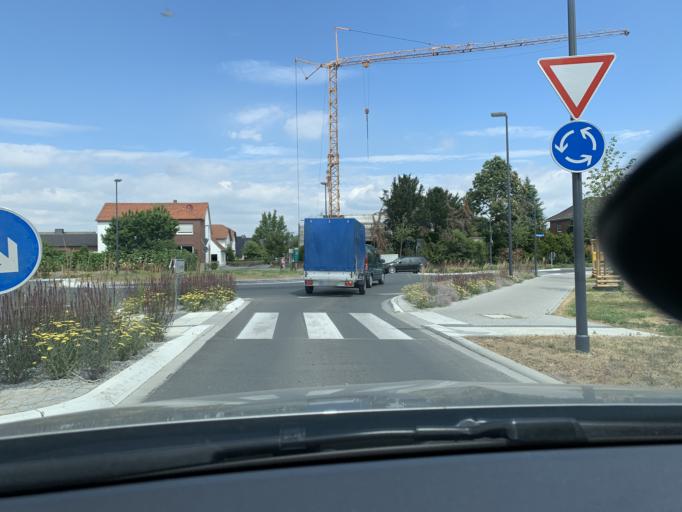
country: DE
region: North Rhine-Westphalia
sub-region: Regierungsbezirk Arnsberg
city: Lippstadt
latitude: 51.6837
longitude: 8.3948
